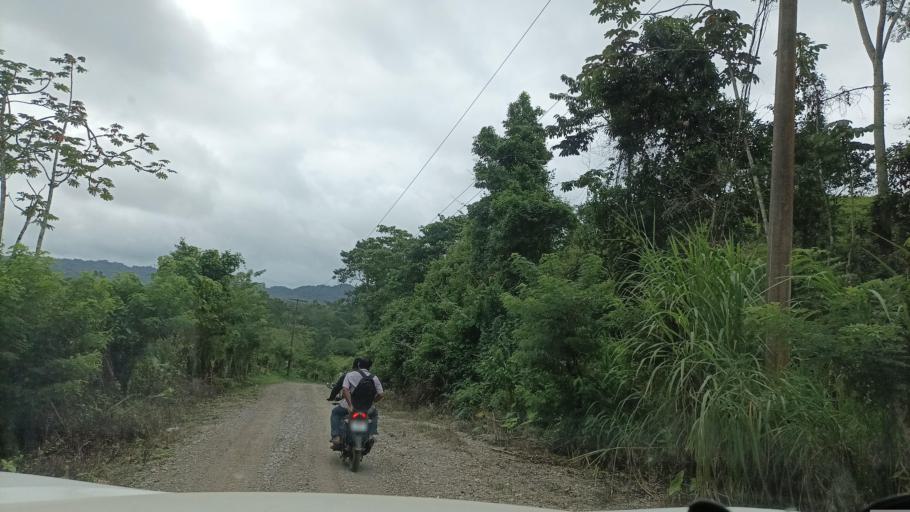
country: MX
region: Veracruz
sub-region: Uxpanapa
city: Poblado 10
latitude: 17.4162
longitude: -94.4182
